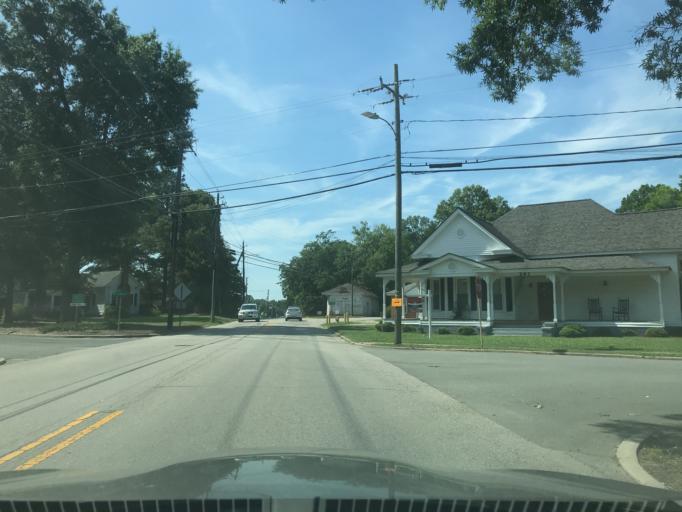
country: US
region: North Carolina
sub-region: Wake County
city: Wendell
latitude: 35.7857
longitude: -78.3739
